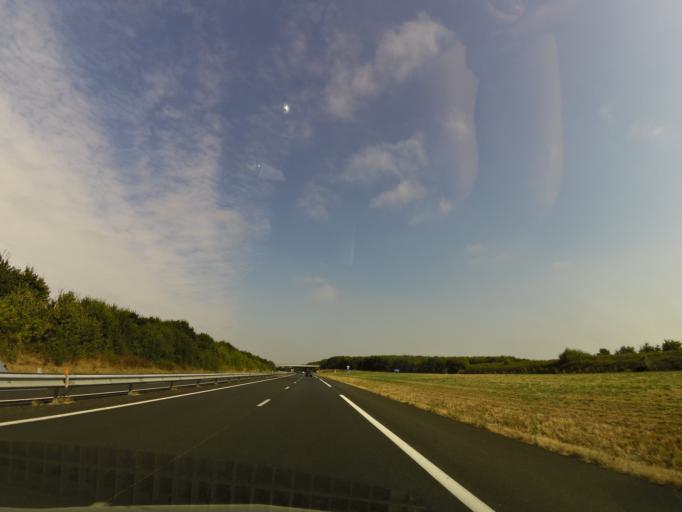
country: FR
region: Pays de la Loire
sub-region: Departement de la Vendee
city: Les Brouzils
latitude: 46.8740
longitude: -1.2857
